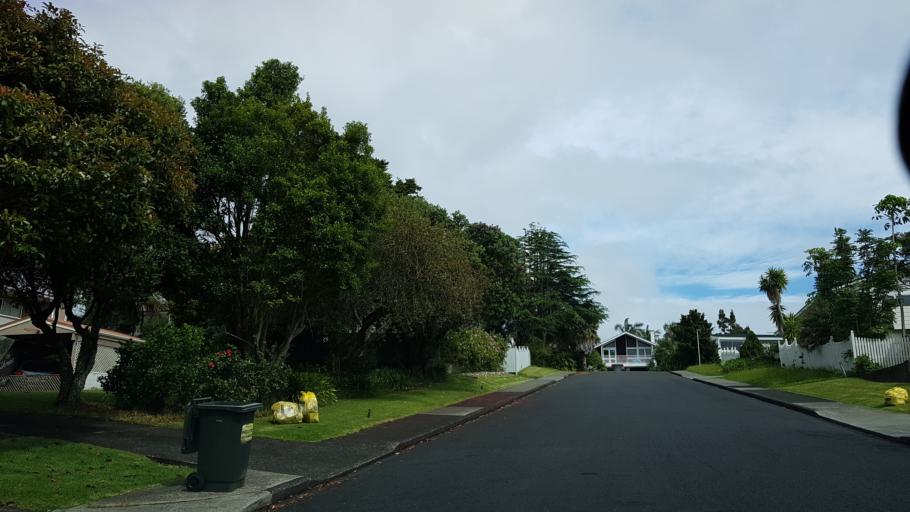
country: NZ
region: Auckland
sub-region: Auckland
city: North Shore
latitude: -36.7898
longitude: 174.7414
